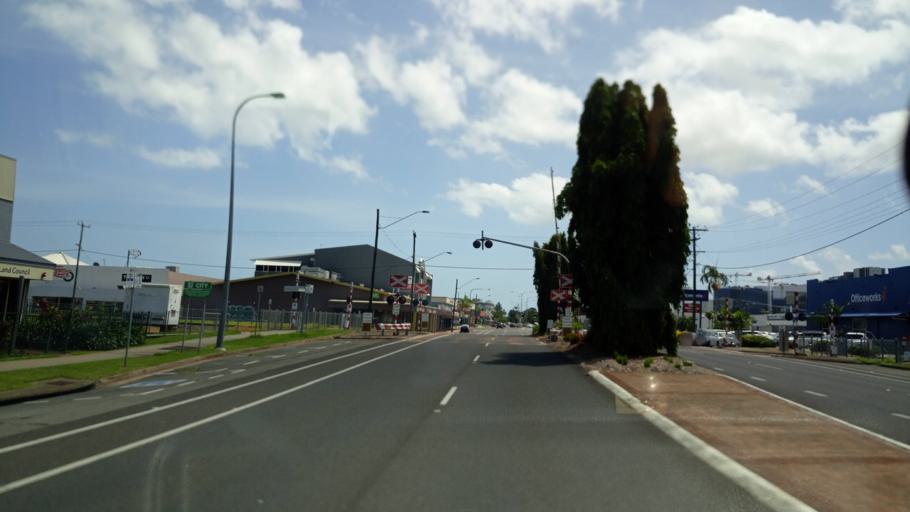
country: AU
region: Queensland
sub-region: Cairns
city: Cairns
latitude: -16.9223
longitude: 145.7682
